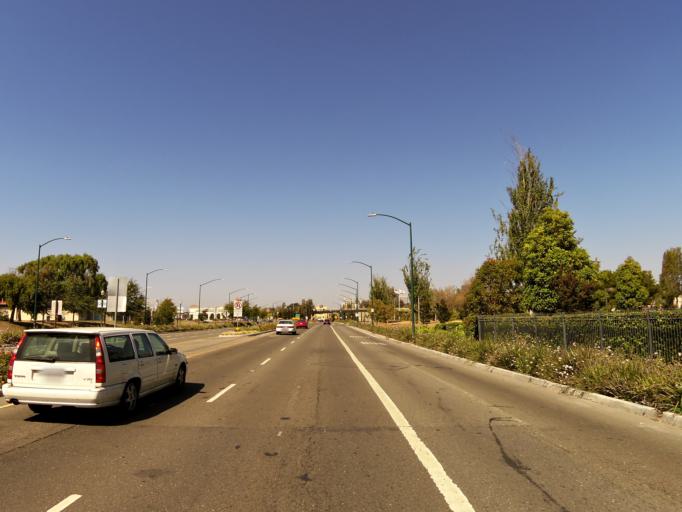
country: US
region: California
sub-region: Alameda County
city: Oakland
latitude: 37.7812
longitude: -122.2765
